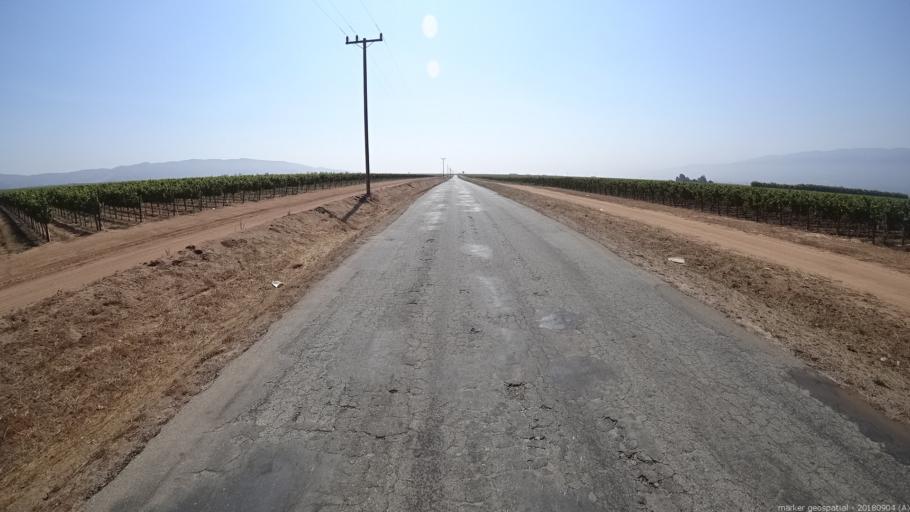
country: US
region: California
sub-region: Monterey County
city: Gonzales
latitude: 36.5092
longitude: -121.4043
